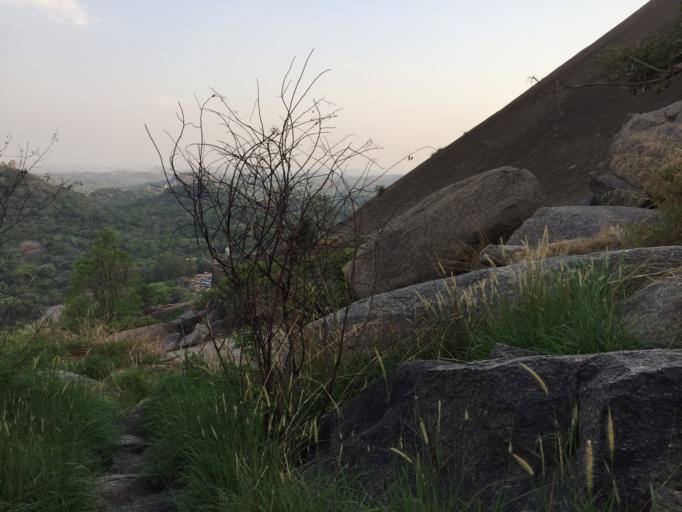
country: IN
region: Karnataka
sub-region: Ramanagara
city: Magadi
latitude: 12.9214
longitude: 77.2981
